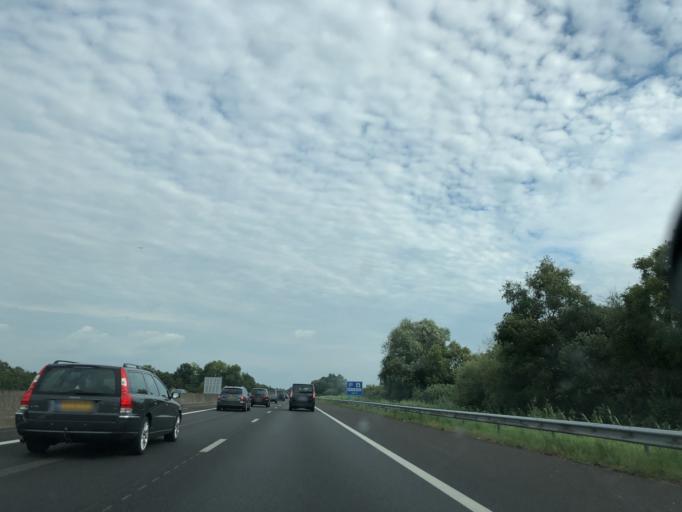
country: NL
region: Groningen
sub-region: Gemeente Haren
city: Haren
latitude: 53.1577
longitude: 6.5967
